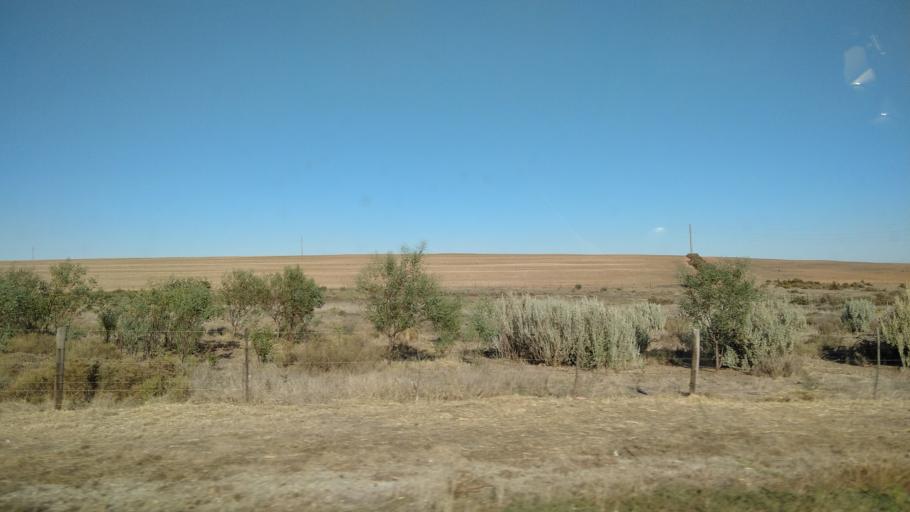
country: ZA
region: Western Cape
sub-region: West Coast District Municipality
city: Malmesbury
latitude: -33.3432
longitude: 18.6375
